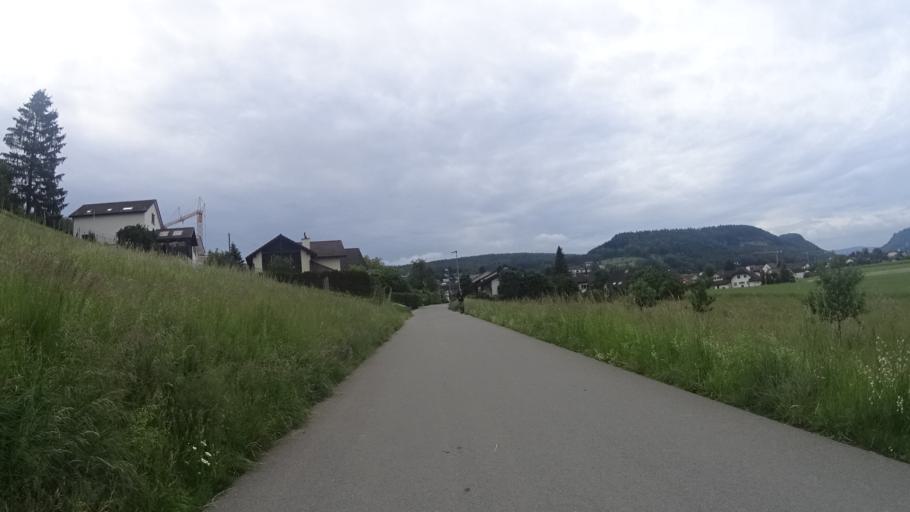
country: CH
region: Aargau
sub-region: Bezirk Baden
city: Wurenlingen
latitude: 47.5405
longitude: 8.2563
